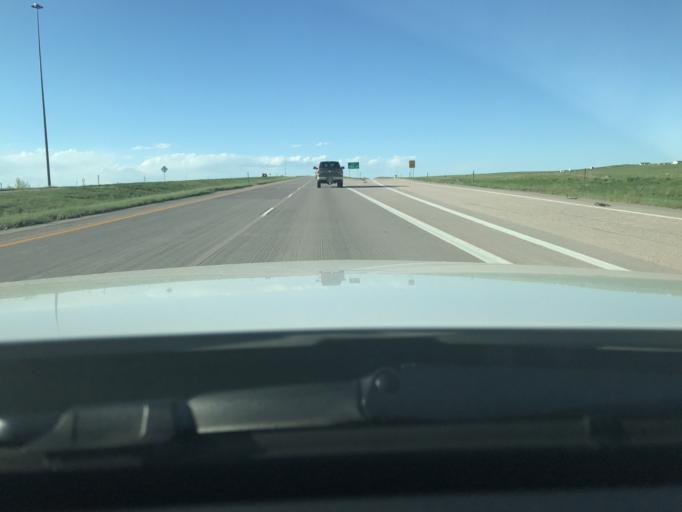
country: US
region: Colorado
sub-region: Larimer County
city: Wellington
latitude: 40.8370
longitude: -104.9674
